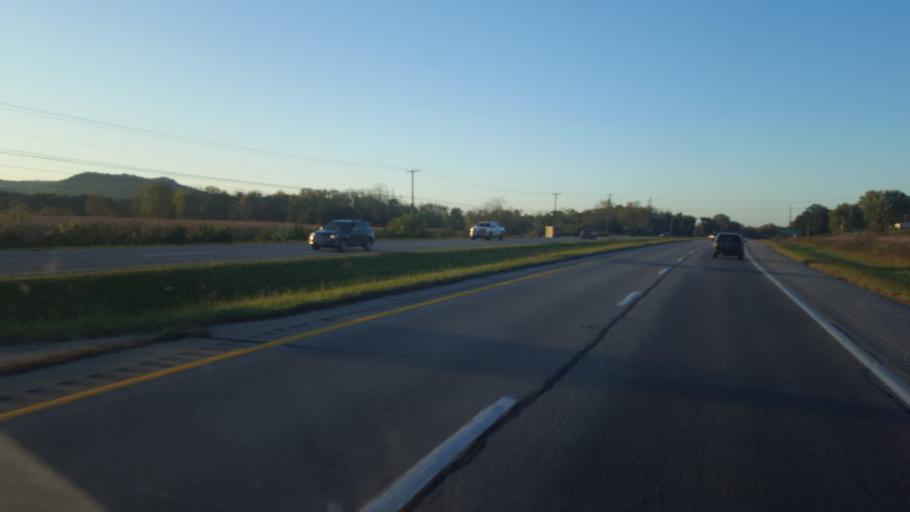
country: US
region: Ohio
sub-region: Scioto County
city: Lucasville
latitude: 38.9244
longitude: -83.0202
